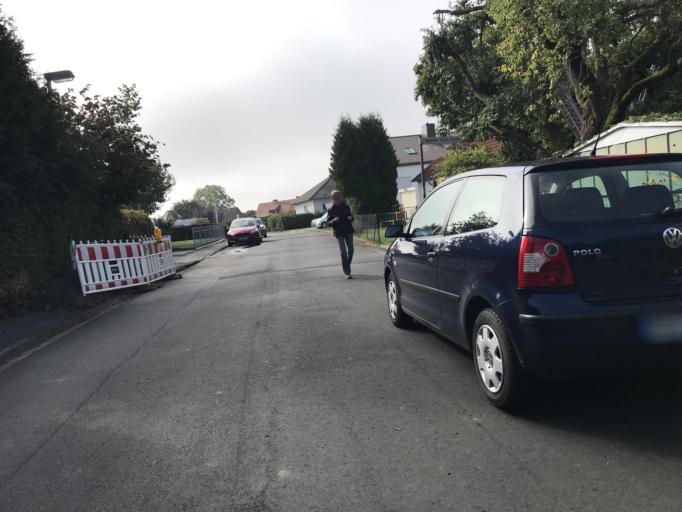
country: DE
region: Hesse
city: Gudensberg
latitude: 51.1805
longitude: 9.3788
